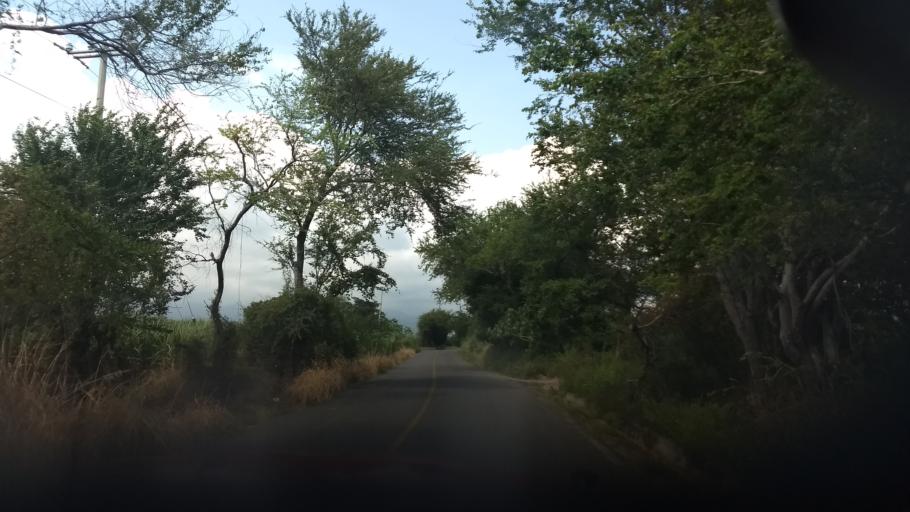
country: MX
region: Jalisco
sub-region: Tonila
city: San Marcos
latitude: 19.4292
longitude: -103.4921
